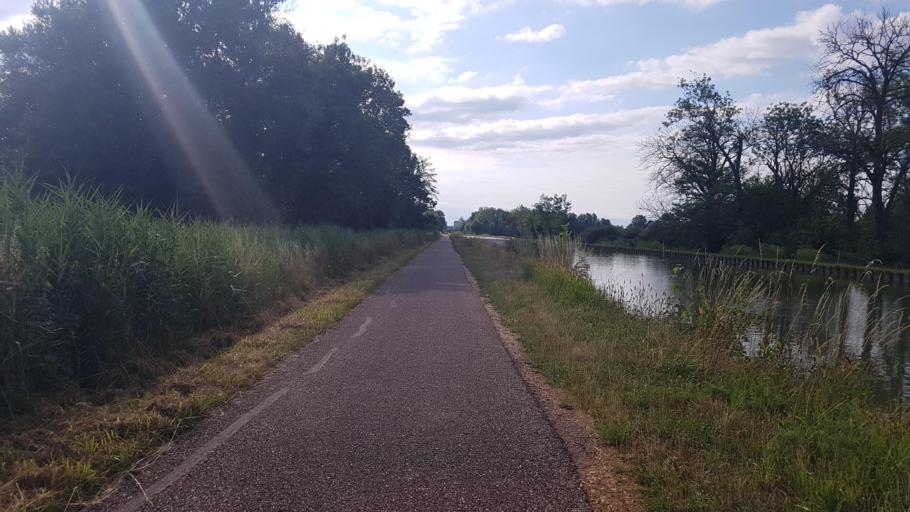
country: FR
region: Alsace
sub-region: Departement du Bas-Rhin
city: Wingersheim
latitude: 48.7329
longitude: 7.6604
